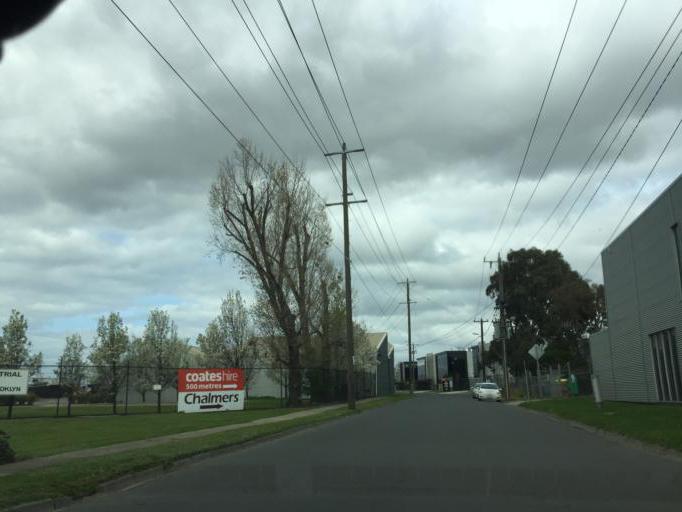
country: AU
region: Victoria
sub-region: Hobsons Bay
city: South Kingsville
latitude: -37.8198
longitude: 144.8604
